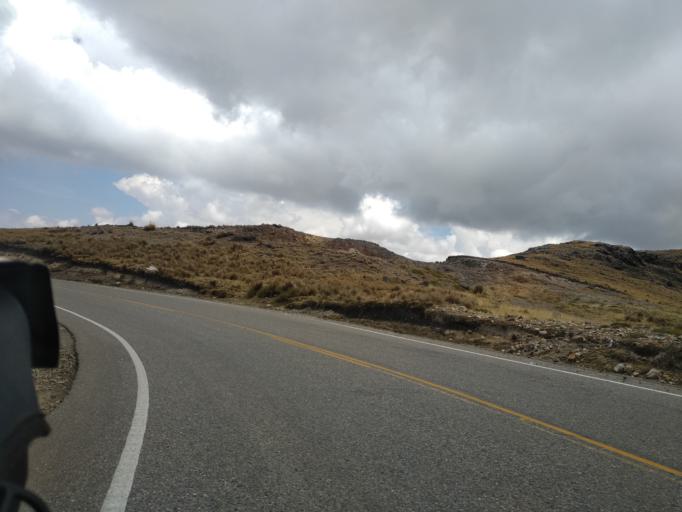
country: PE
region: La Libertad
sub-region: Provincia de Santiago de Chuco
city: Quiruvilca
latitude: -7.9713
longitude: -78.2071
